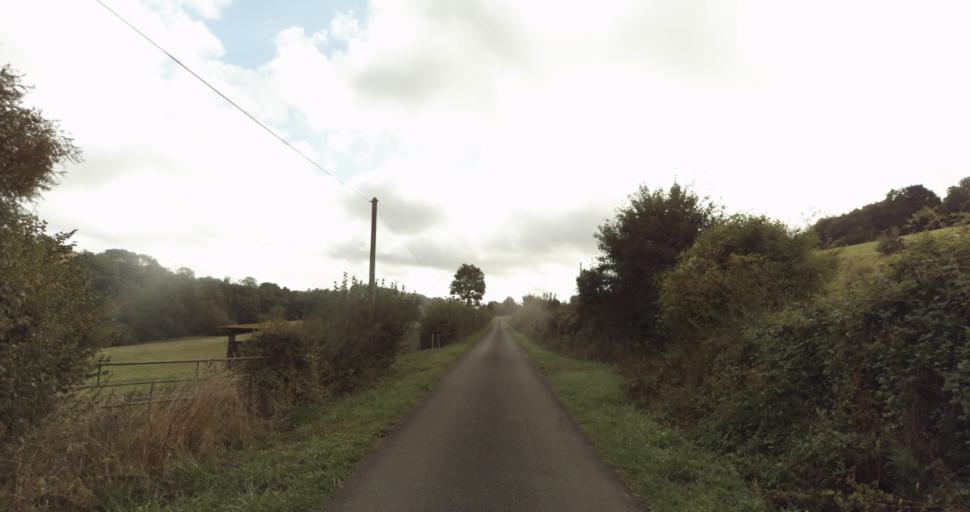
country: FR
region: Lower Normandy
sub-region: Departement de l'Orne
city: Gace
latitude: 48.8441
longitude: 0.2935
